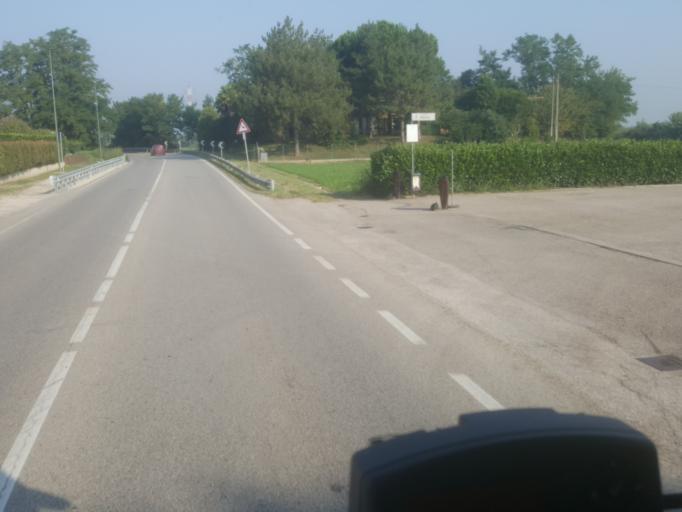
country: IT
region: Emilia-Romagna
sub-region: Provincia di Ravenna
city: Fornace Zarattini
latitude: 44.4441
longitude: 12.1335
